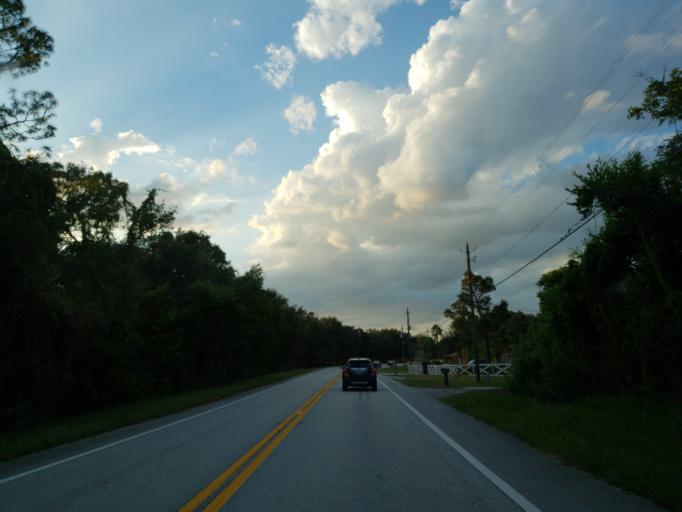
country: US
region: Florida
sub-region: Pasco County
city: Odessa
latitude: 28.1598
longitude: -82.5861
